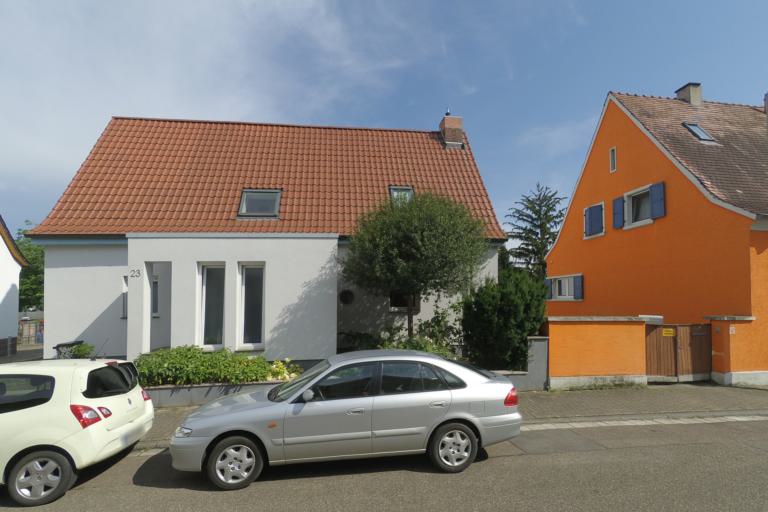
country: DE
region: Rheinland-Pfalz
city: Altrip
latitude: 49.4295
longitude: 8.4989
